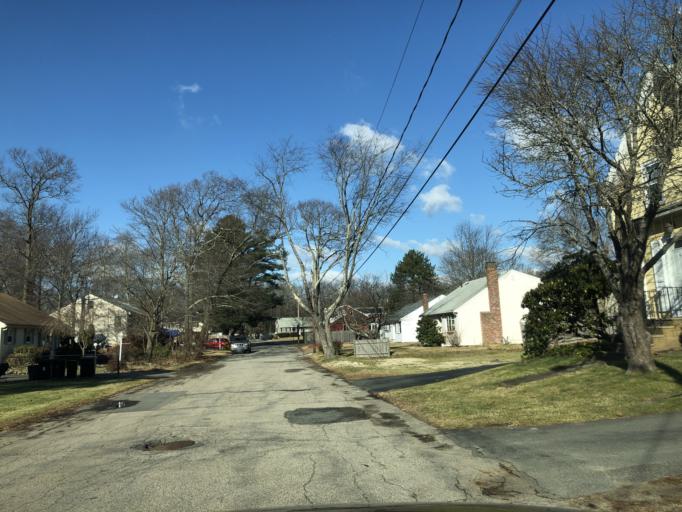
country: US
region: Massachusetts
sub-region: Plymouth County
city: Brockton
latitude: 42.1135
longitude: -71.0132
